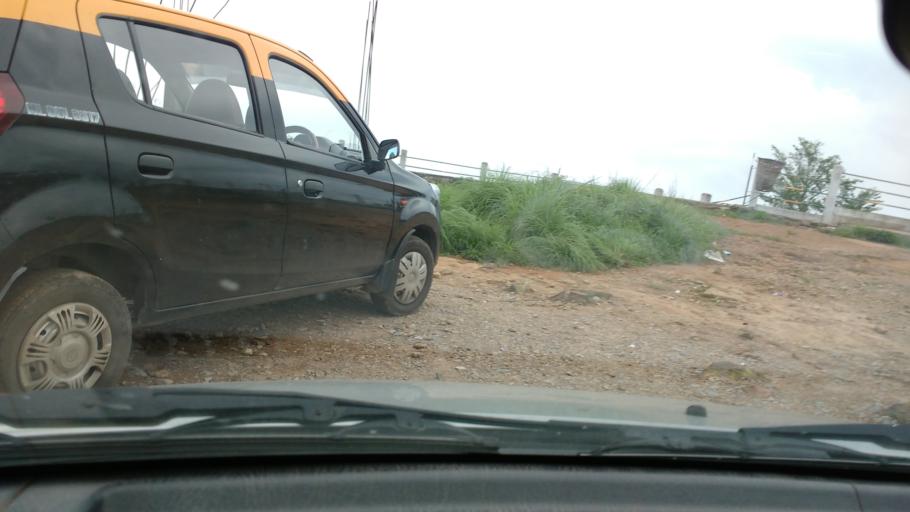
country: IN
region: Meghalaya
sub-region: East Khasi Hills
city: Cherrapunji
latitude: 25.2721
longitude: 91.6904
